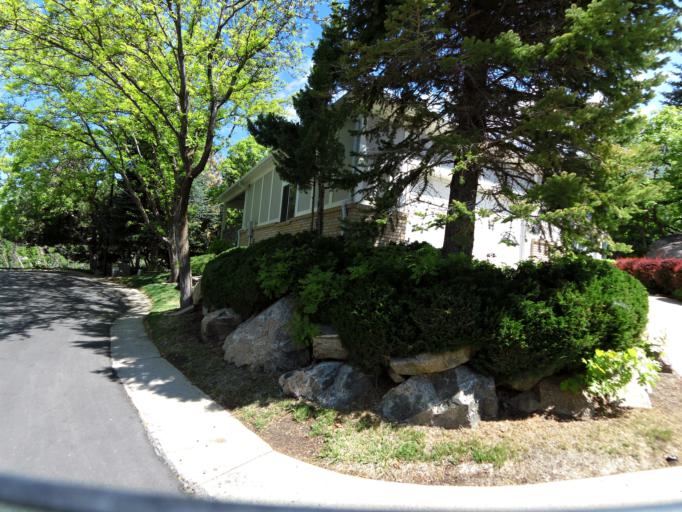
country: US
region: Utah
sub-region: Weber County
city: Uintah
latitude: 41.1784
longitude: -111.9350
